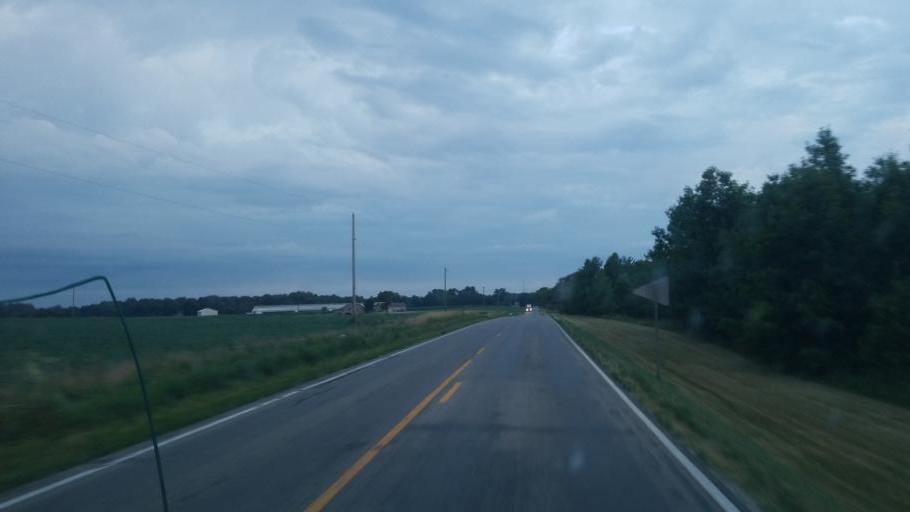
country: US
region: Ohio
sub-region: Defiance County
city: Hicksville
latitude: 41.3398
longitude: -84.8278
